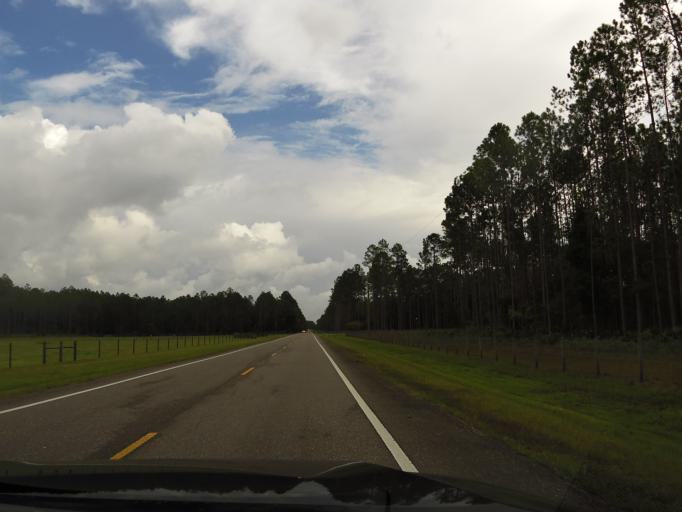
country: US
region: Florida
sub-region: Duval County
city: Baldwin
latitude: 30.3732
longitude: -81.9343
